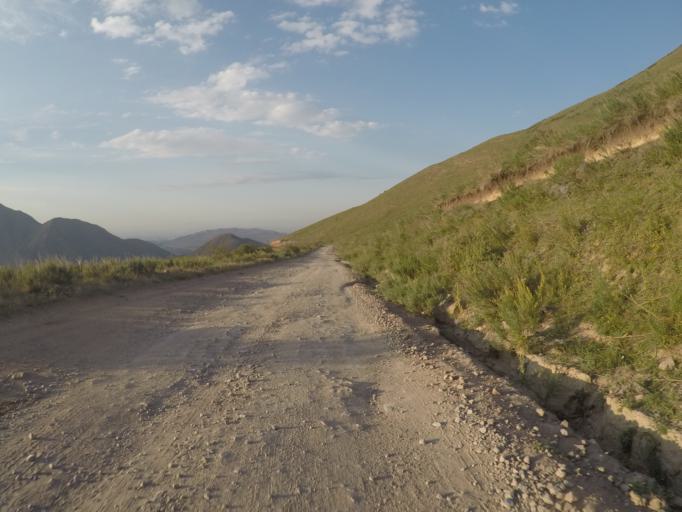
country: KG
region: Chuy
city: Bishkek
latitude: 42.6527
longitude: 74.6620
